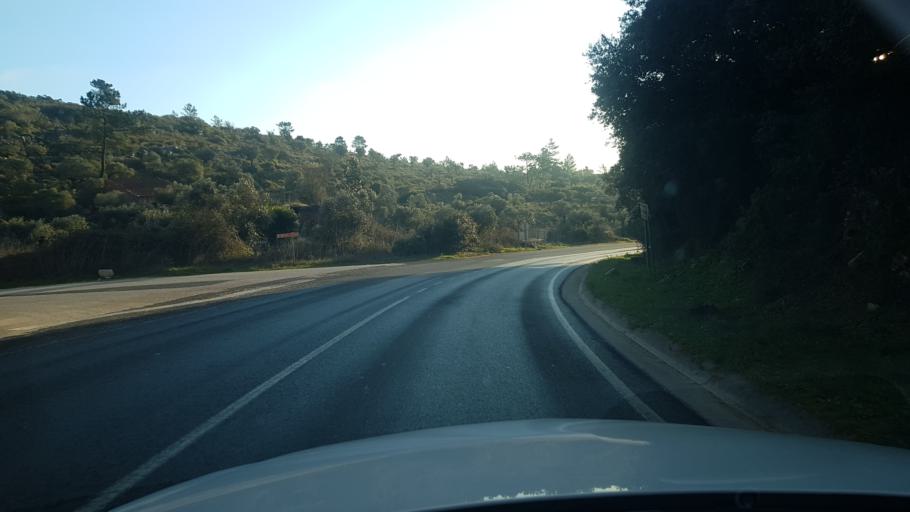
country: PT
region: Santarem
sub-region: Ourem
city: Ourem
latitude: 39.5730
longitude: -8.5883
